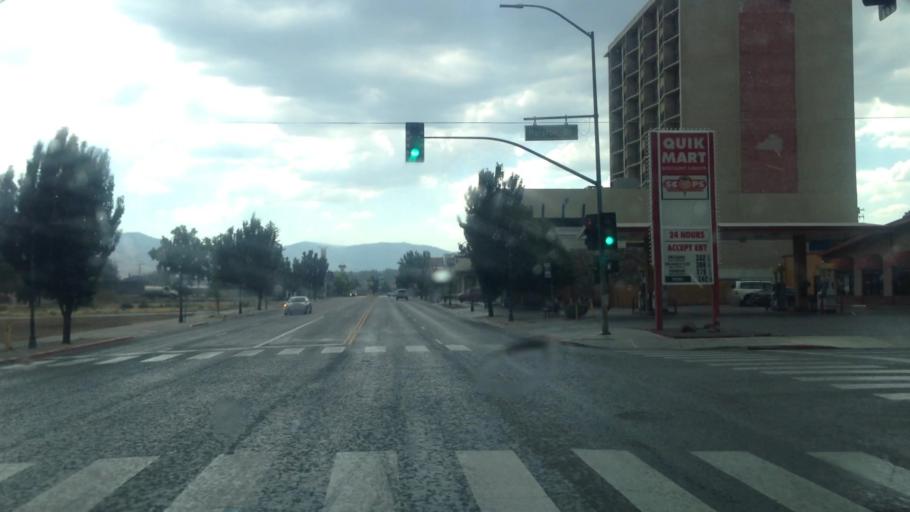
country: US
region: Nevada
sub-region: Washoe County
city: Reno
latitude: 39.5288
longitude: -119.8206
